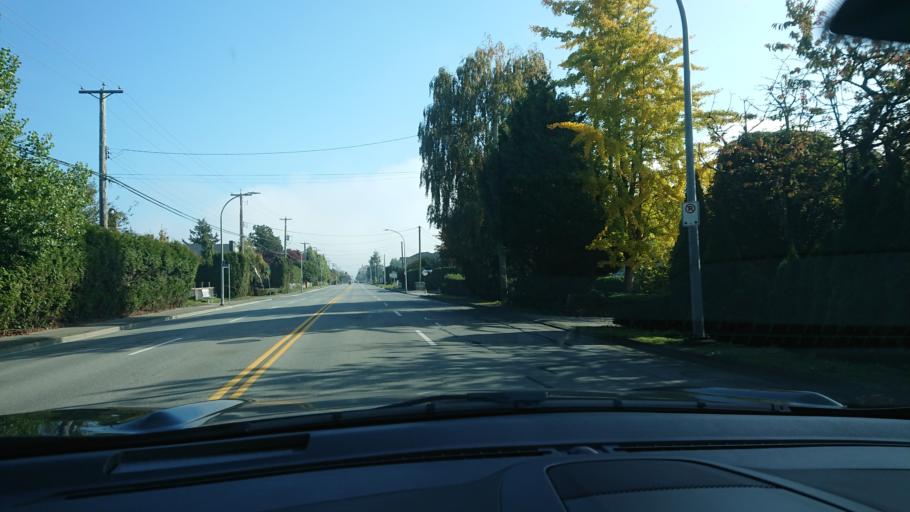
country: CA
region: British Columbia
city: Richmond
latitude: 49.1335
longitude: -123.1562
